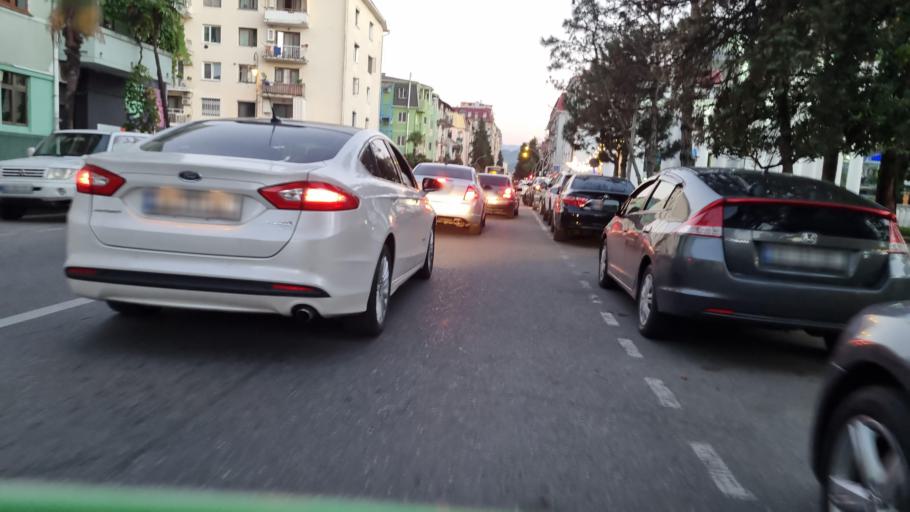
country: GE
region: Ajaria
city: Batumi
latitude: 41.6483
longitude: 41.6297
